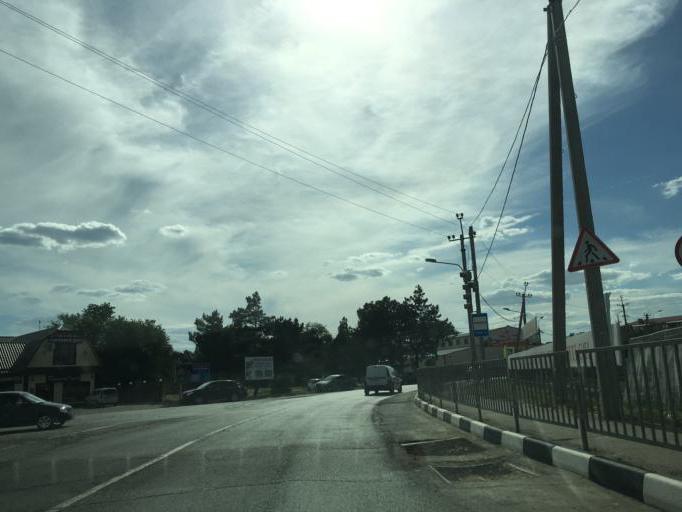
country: RU
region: Krasnodarskiy
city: Kushchevskaya
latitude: 46.5654
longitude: 39.6373
